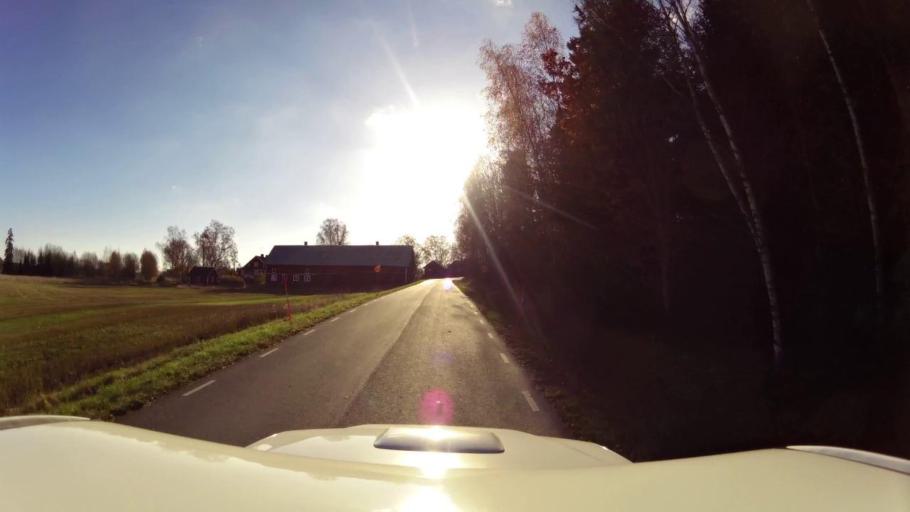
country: SE
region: OEstergoetland
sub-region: Linkopings Kommun
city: Linghem
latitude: 58.4451
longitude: 15.7827
